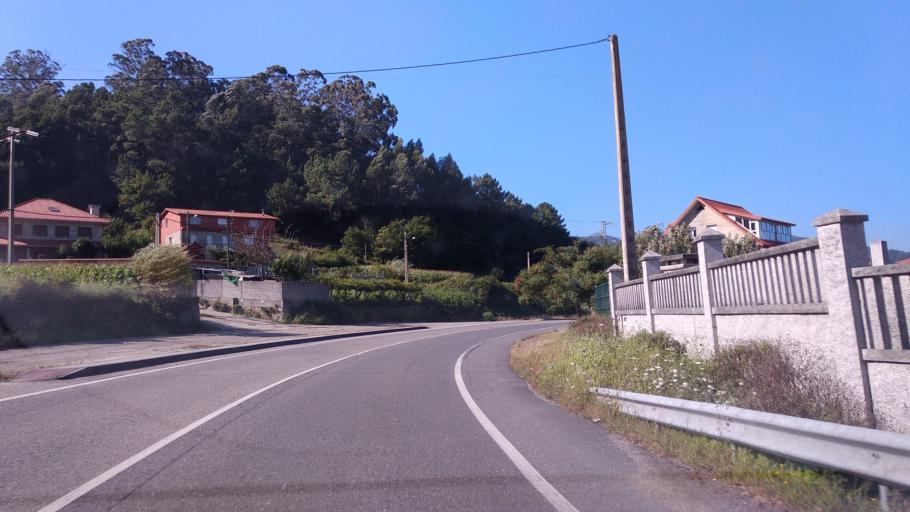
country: ES
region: Galicia
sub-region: Provincia de Pontevedra
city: Redondela
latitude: 42.3099
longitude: -8.6627
